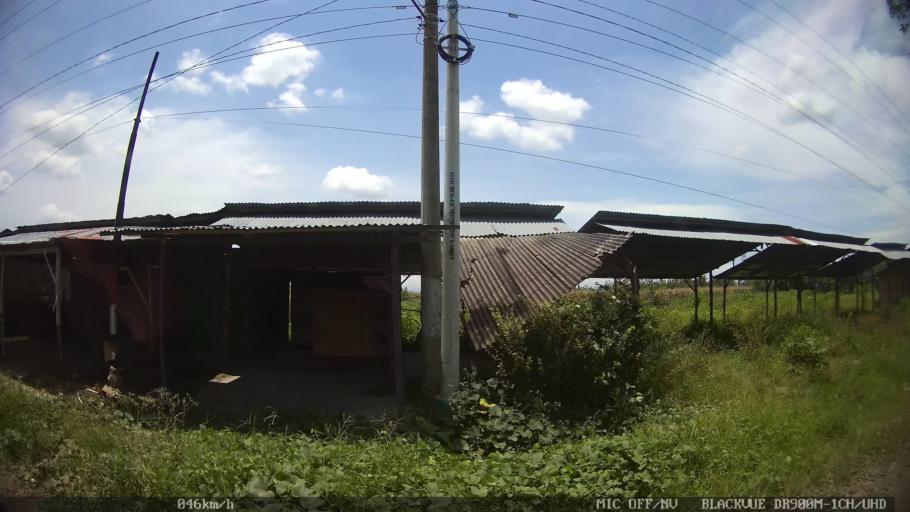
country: ID
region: North Sumatra
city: Binjai
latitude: 3.5912
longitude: 98.5169
